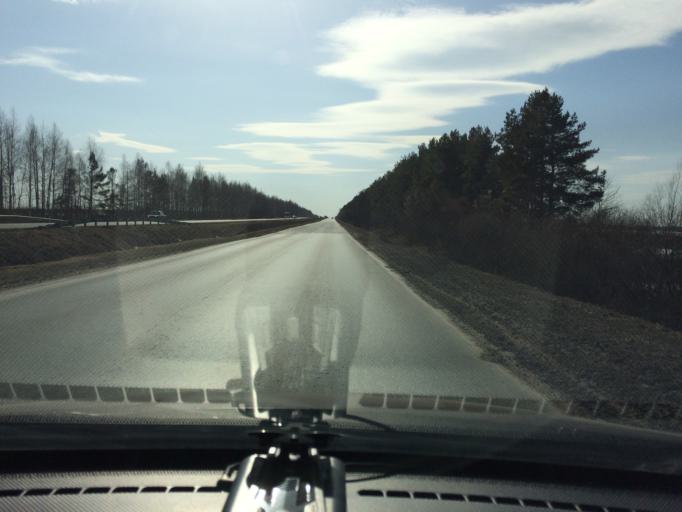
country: RU
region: Mariy-El
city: Yoshkar-Ola
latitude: 56.7293
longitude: 48.1400
